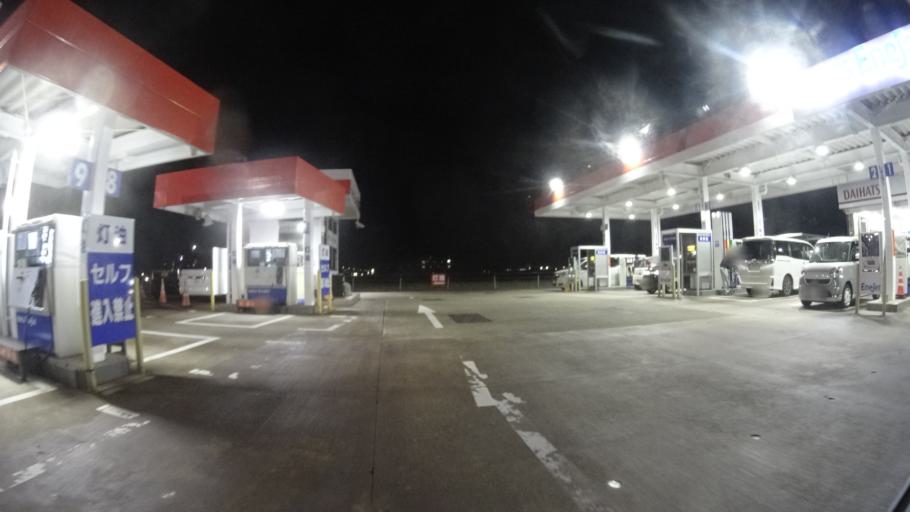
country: JP
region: Niigata
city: Yoshida-kasugacho
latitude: 37.6738
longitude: 138.8779
